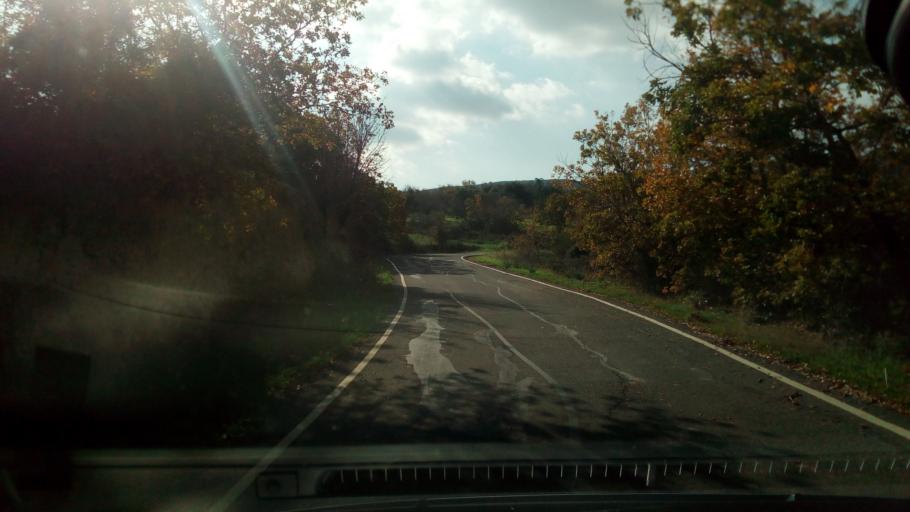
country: CY
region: Pafos
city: Polis
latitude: 34.9581
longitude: 32.4311
